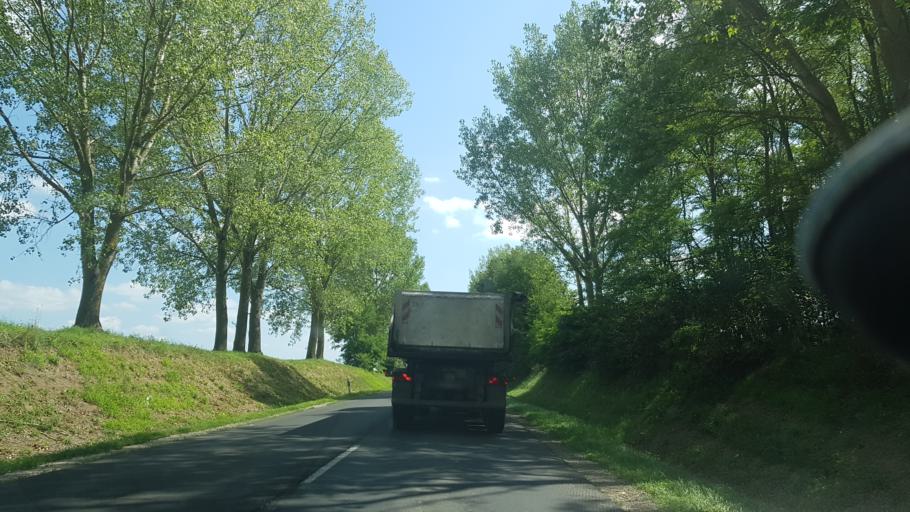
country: HU
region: Somogy
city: Kethely
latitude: 46.6220
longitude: 17.3972
